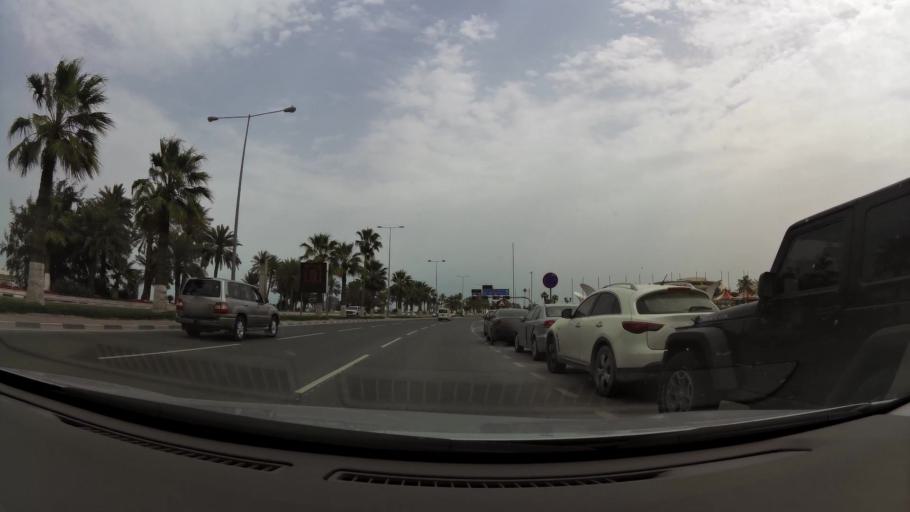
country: QA
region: Baladiyat ad Dawhah
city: Doha
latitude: 25.2910
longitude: 51.5478
